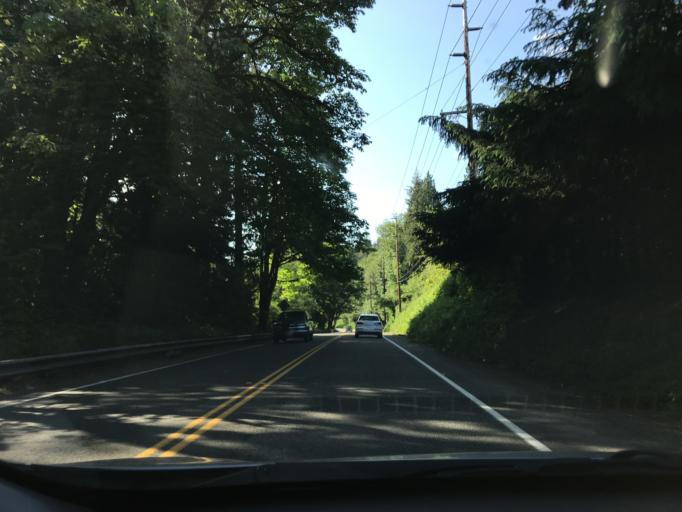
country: US
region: Washington
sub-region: King County
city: Mirrormont
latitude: 47.4552
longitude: -121.9998
